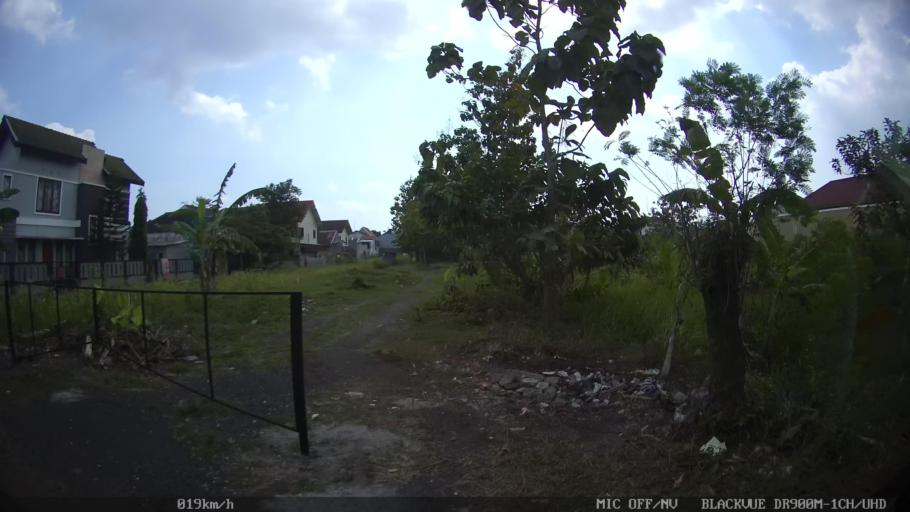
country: ID
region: Daerah Istimewa Yogyakarta
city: Yogyakarta
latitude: -7.8162
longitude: 110.4060
